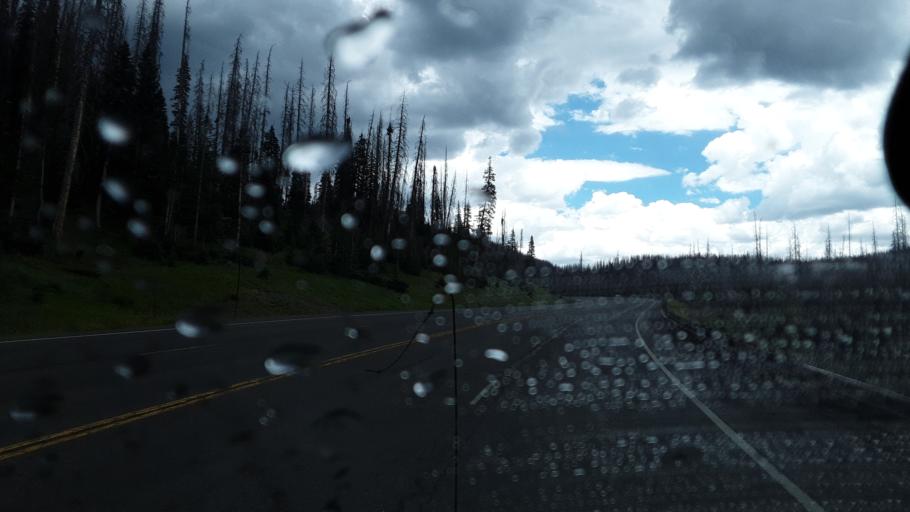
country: US
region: Colorado
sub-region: Archuleta County
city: Pagosa Springs
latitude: 37.4867
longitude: -106.8336
